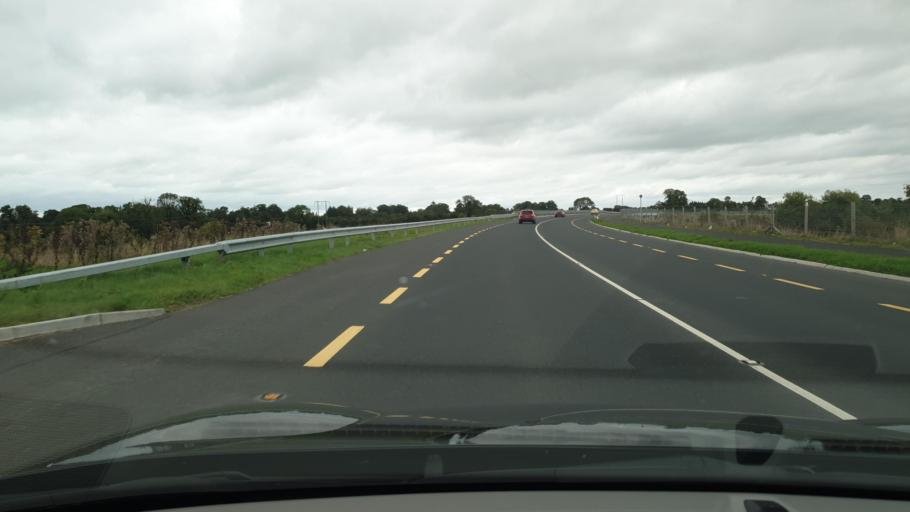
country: IE
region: Leinster
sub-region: Kildare
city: Sallins
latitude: 53.2579
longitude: -6.6794
